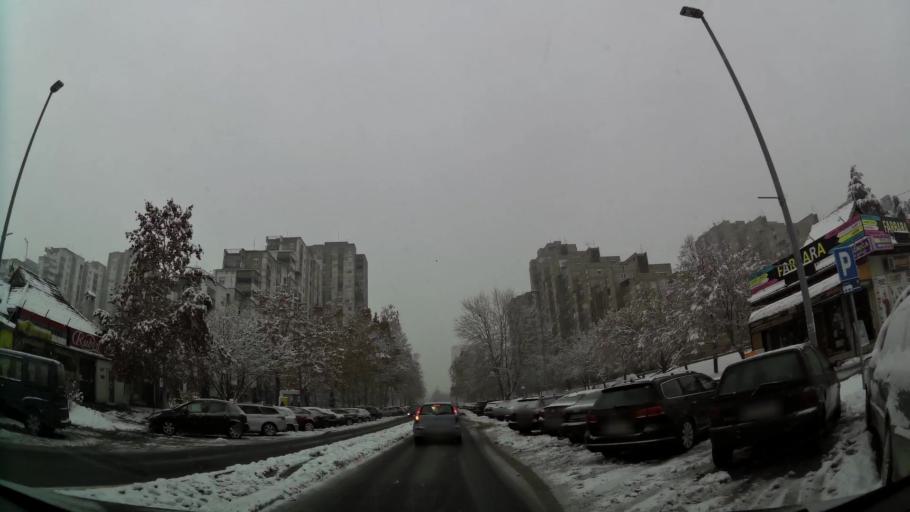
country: RS
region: Central Serbia
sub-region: Belgrade
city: Novi Beograd
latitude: 44.8024
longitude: 20.3806
